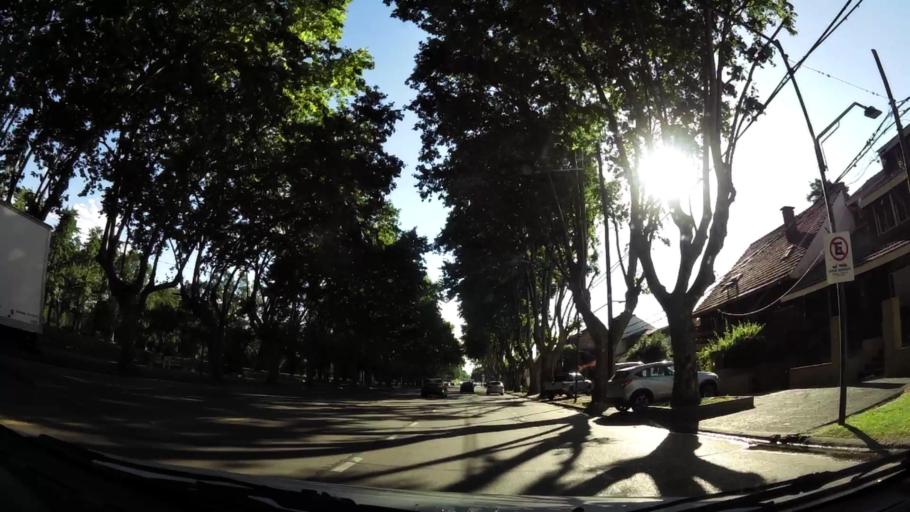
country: AR
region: Buenos Aires
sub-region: Partido de San Isidro
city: San Isidro
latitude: -34.4808
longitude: -58.5254
